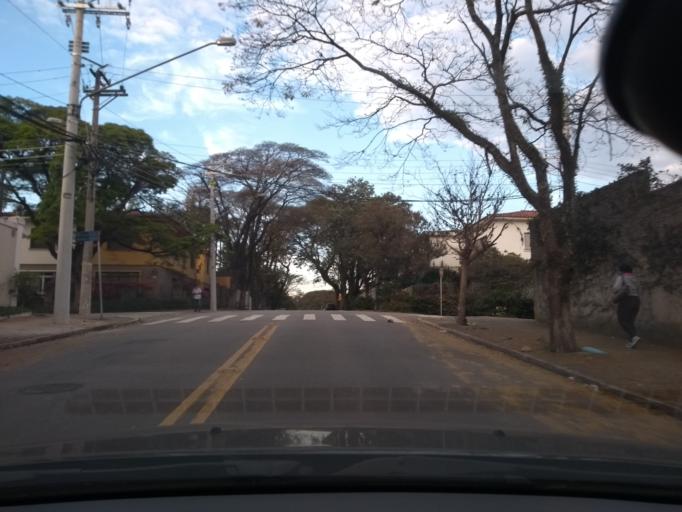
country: BR
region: Sao Paulo
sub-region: Sao Paulo
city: Sao Paulo
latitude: -23.5432
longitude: -46.6745
